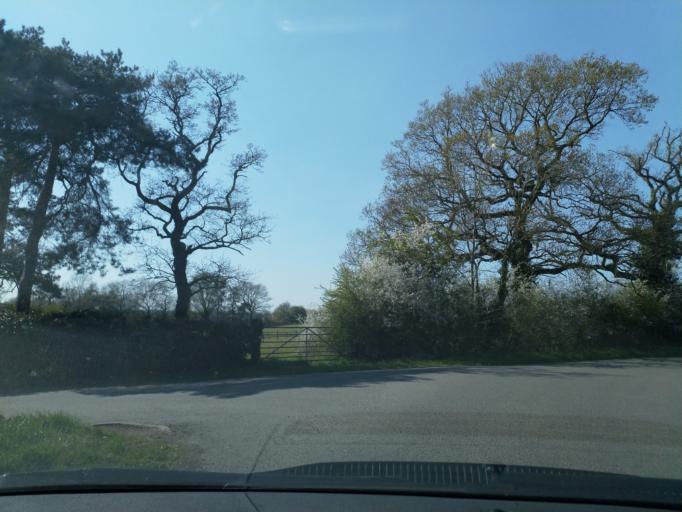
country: GB
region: England
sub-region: Warwickshire
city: Wroxall
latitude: 52.2862
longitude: -1.6705
